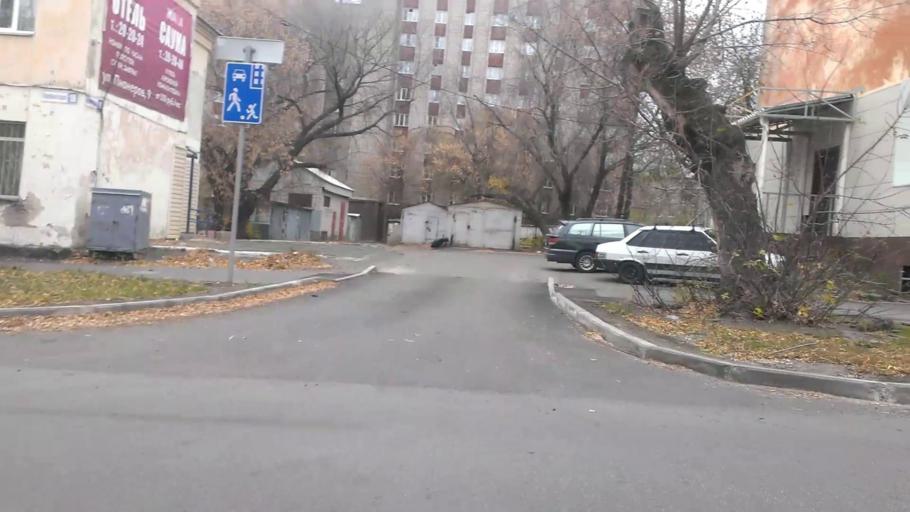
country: RU
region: Altai Krai
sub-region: Gorod Barnaulskiy
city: Barnaul
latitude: 53.3540
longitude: 83.7634
